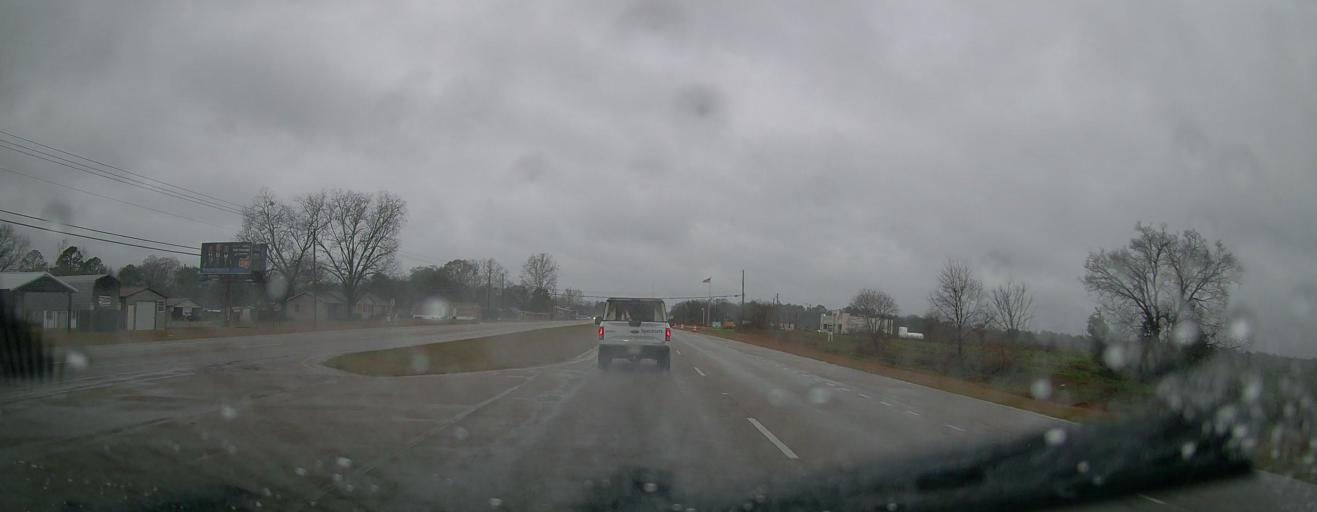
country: US
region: Alabama
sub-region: Autauga County
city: Prattville
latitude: 32.4348
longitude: -86.4209
